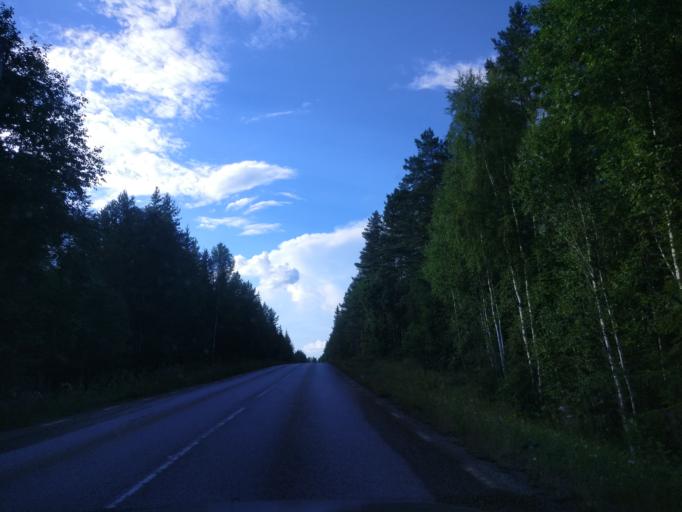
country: SE
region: Dalarna
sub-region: Ludvika Kommun
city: Ludvika
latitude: 60.2866
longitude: 15.1411
